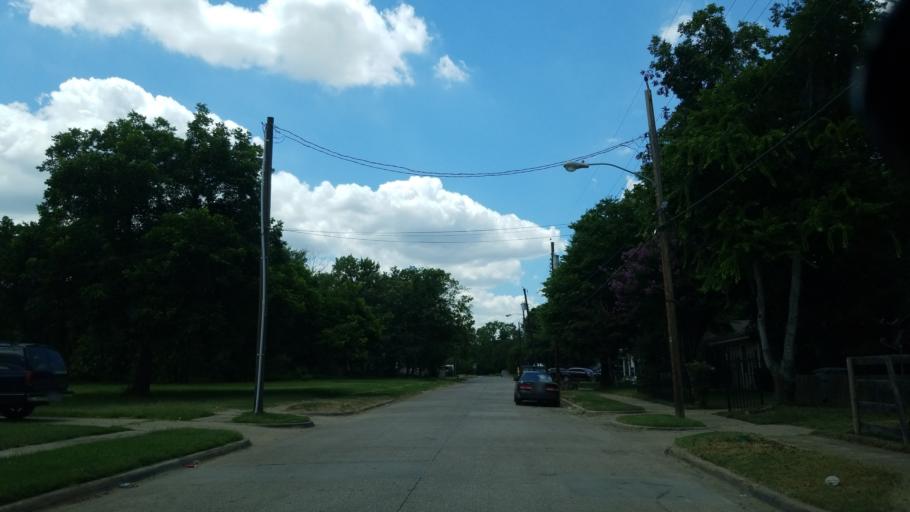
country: US
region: Texas
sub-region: Dallas County
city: Dallas
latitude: 32.7419
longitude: -96.7513
